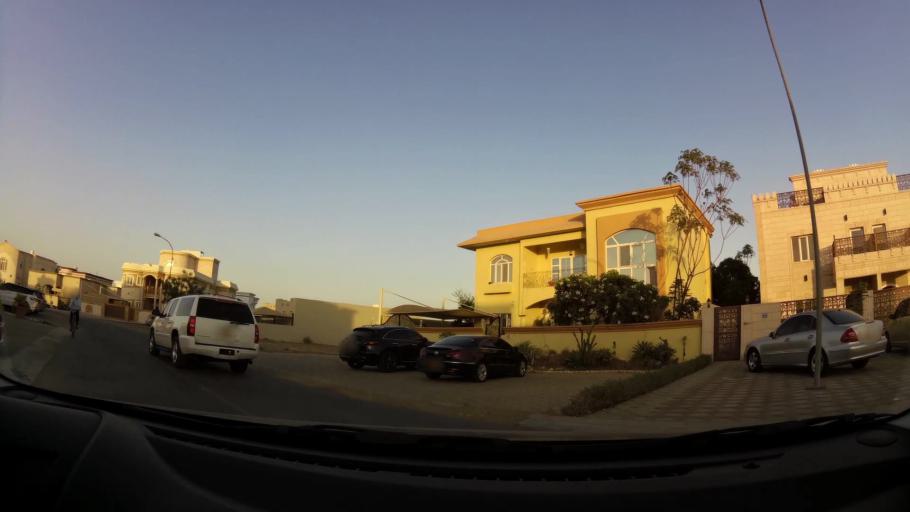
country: OM
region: Muhafazat Masqat
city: As Sib al Jadidah
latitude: 23.6121
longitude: 58.2017
